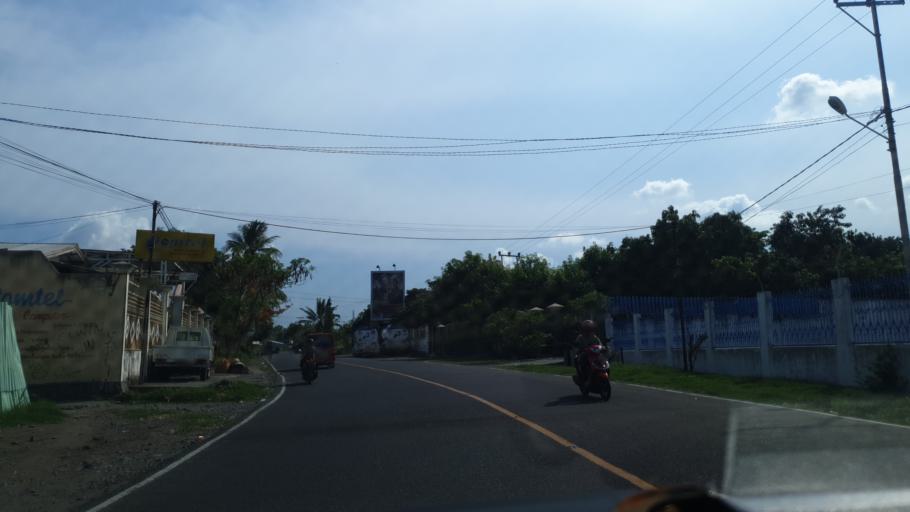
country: ID
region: East Nusa Tenggara
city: Nangalimang
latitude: -8.6359
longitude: 122.2093
